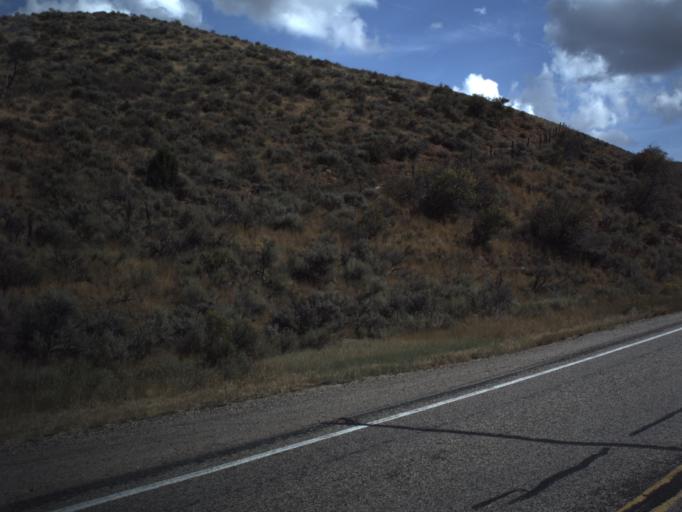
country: US
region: Utah
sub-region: Rich County
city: Randolph
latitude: 41.8206
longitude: -111.2886
